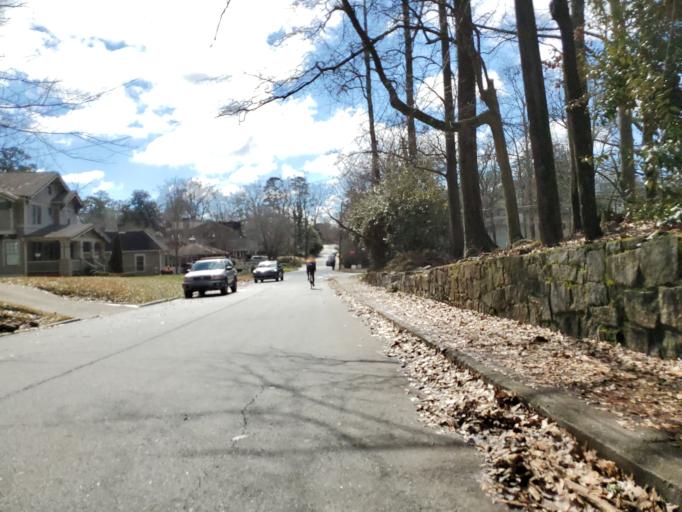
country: US
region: Georgia
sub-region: DeKalb County
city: Decatur
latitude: 33.7637
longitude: -84.3019
